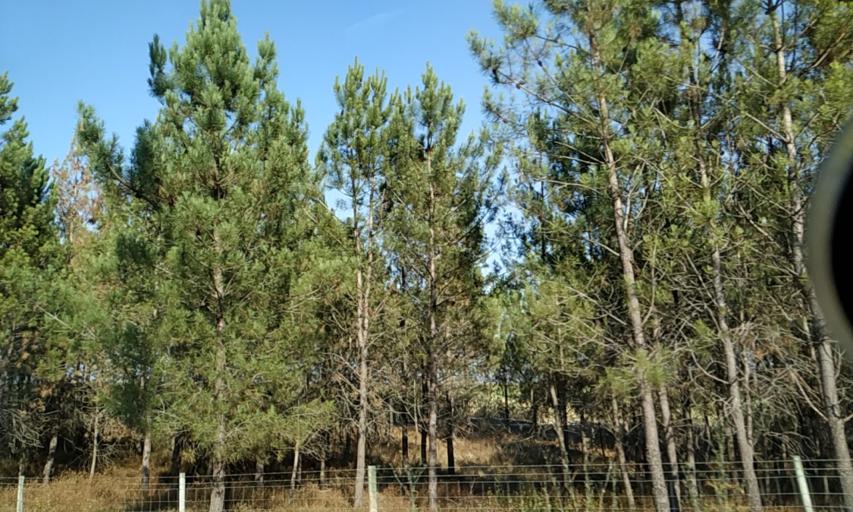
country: PT
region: Santarem
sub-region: Coruche
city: Coruche
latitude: 39.0322
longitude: -8.5610
